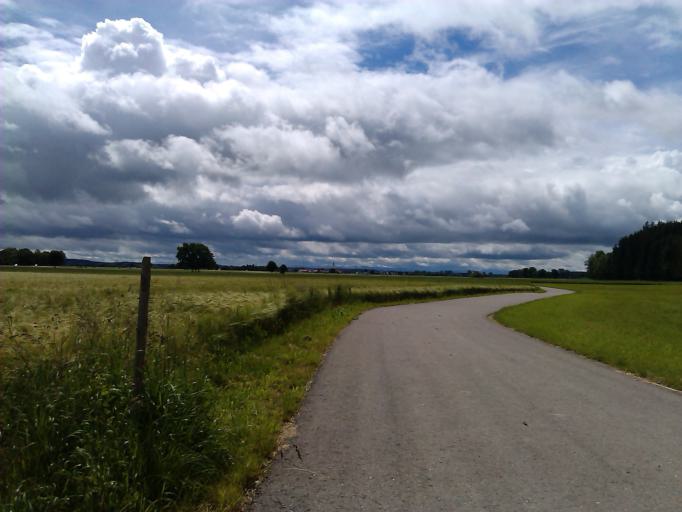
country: DE
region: Bavaria
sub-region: Swabia
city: Bad Worishofen
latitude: 47.9900
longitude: 10.6054
